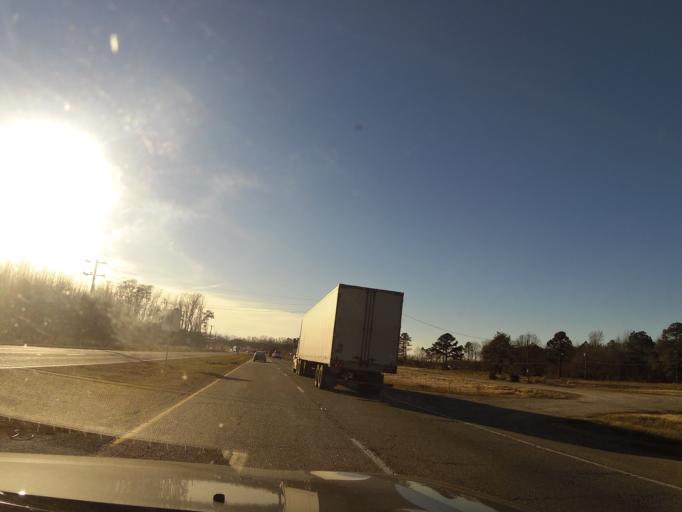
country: US
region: Virginia
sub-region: City of Suffolk
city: South Suffolk
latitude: 36.7133
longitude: -76.6699
